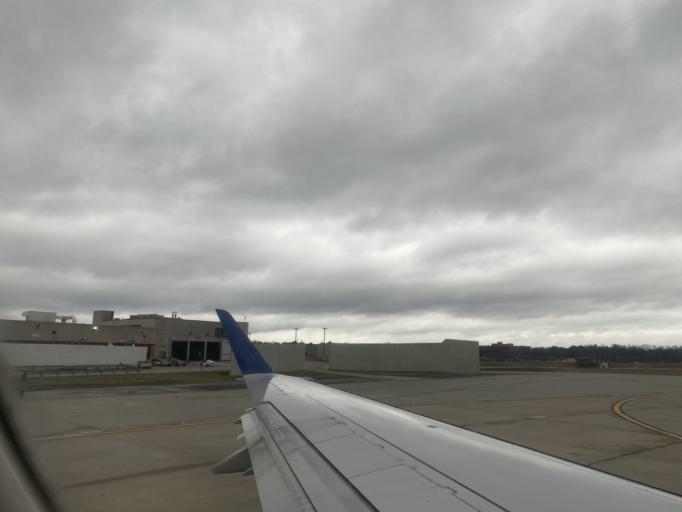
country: US
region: Georgia
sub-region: Fulton County
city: College Park
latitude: 33.6440
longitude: -84.4410
